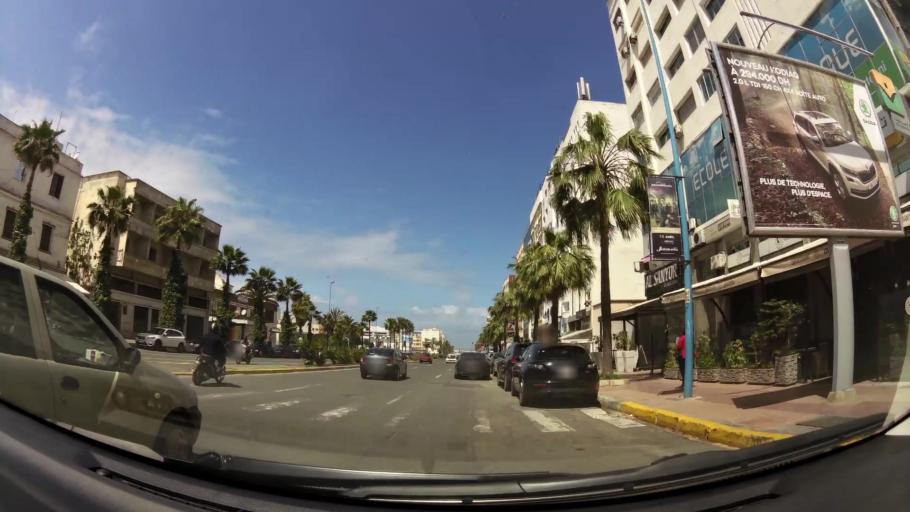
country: MA
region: Grand Casablanca
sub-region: Casablanca
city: Casablanca
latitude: 33.5986
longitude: -7.6386
